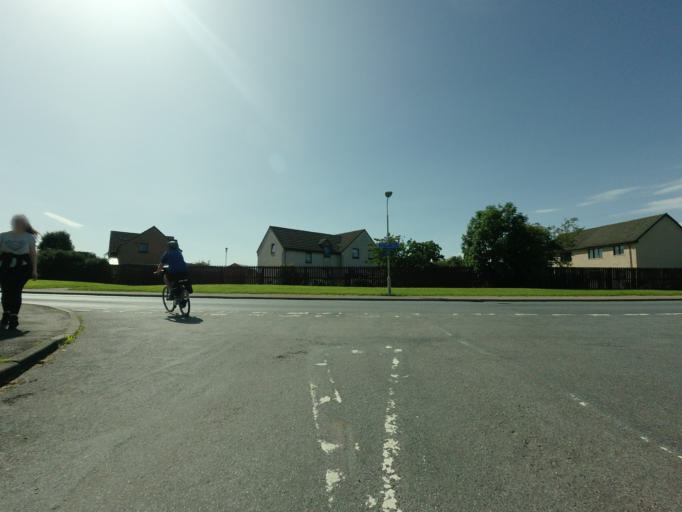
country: GB
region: Scotland
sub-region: Highland
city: Inverness
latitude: 57.4834
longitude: -4.1489
